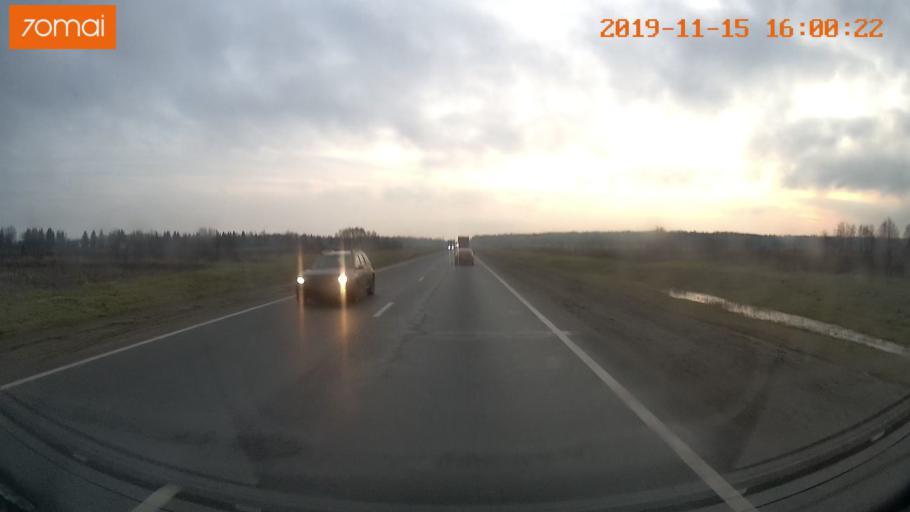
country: RU
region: Jaroslavl
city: Yaroslavl
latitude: 57.7968
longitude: 39.9392
